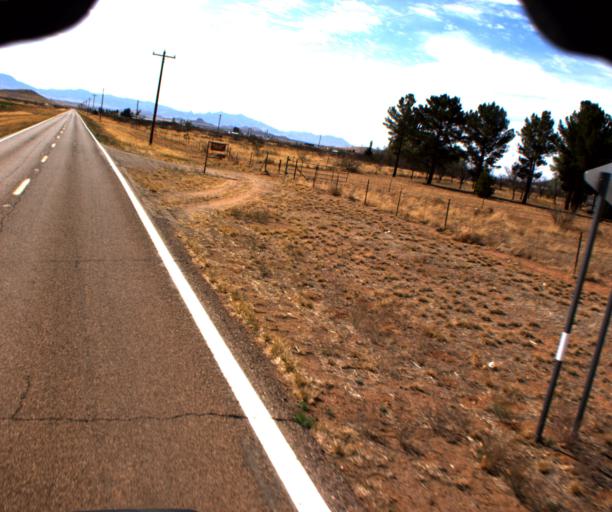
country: US
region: Arizona
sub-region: Cochise County
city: Willcox
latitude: 31.8765
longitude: -109.6449
